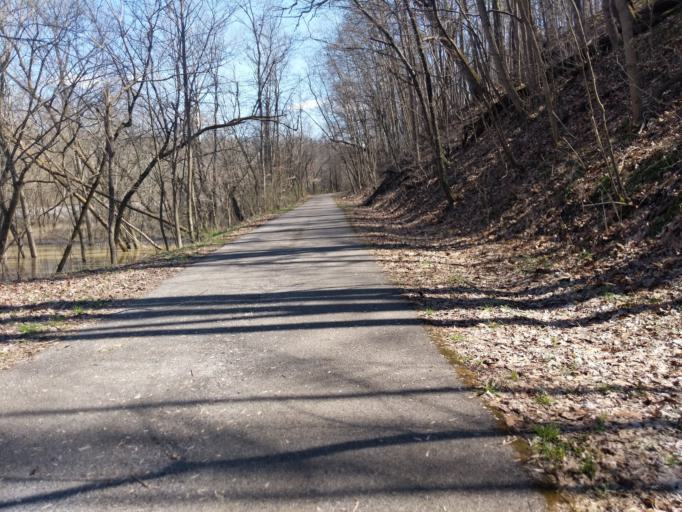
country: US
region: Ohio
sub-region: Athens County
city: Athens
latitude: 39.3512
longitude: -82.1039
